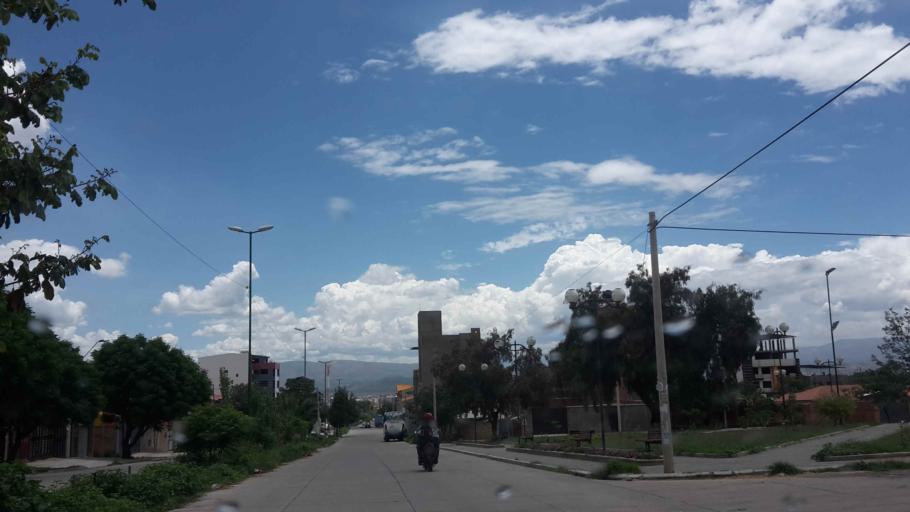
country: BO
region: Cochabamba
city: Cochabamba
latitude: -17.3547
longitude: -66.1836
